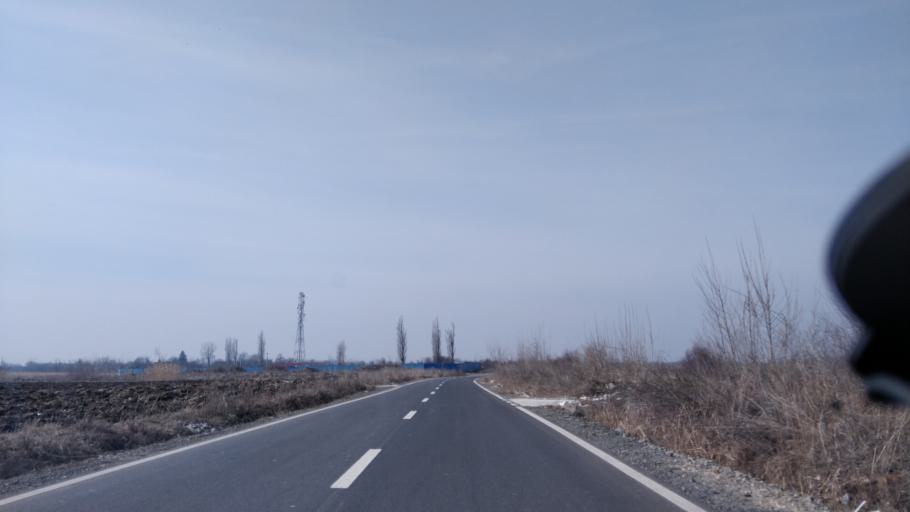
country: RO
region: Giurgiu
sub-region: Comuna Bolintin Deal
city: Bolintin Deal
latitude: 44.4634
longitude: 25.7963
